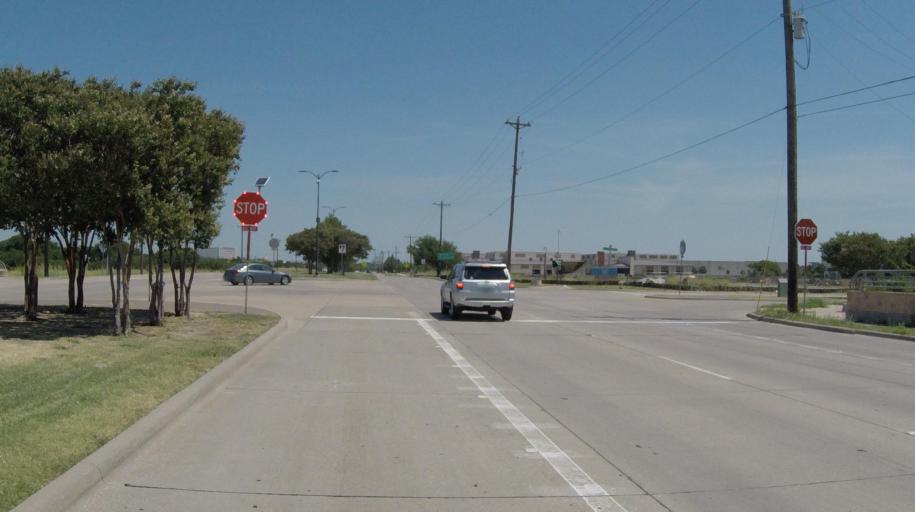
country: US
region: Texas
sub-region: Collin County
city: Frisco
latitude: 33.1634
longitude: -96.8336
